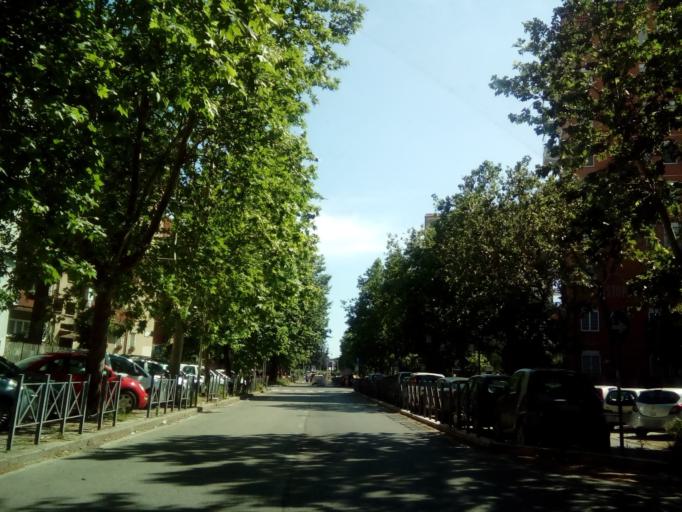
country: IT
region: Latium
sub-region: Citta metropolitana di Roma Capitale
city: Rome
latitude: 41.8580
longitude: 12.5536
